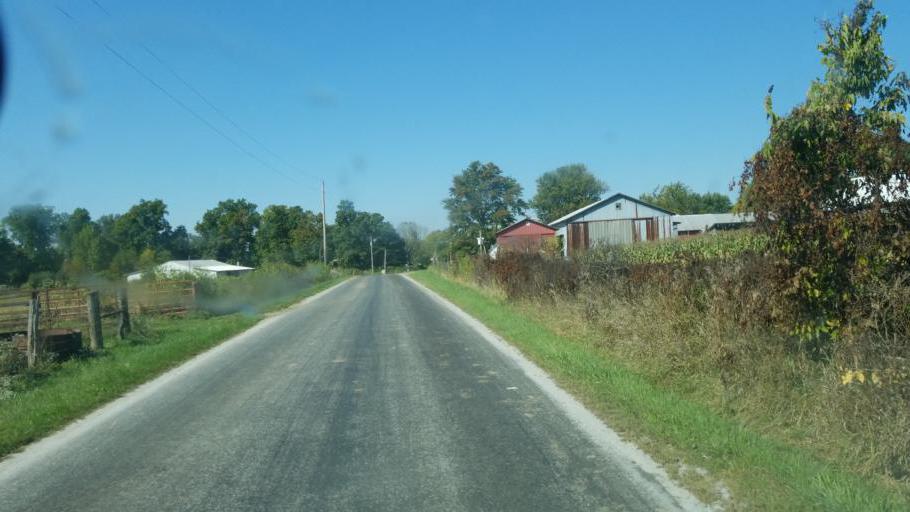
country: US
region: Ohio
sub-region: Hardin County
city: Kenton
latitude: 40.6185
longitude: -83.4962
